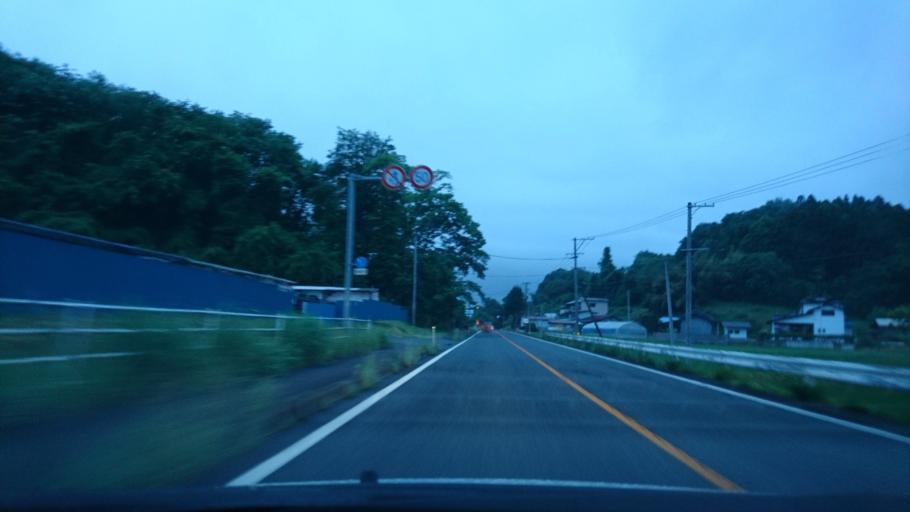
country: JP
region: Iwate
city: Ichinoseki
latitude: 38.7851
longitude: 141.0493
